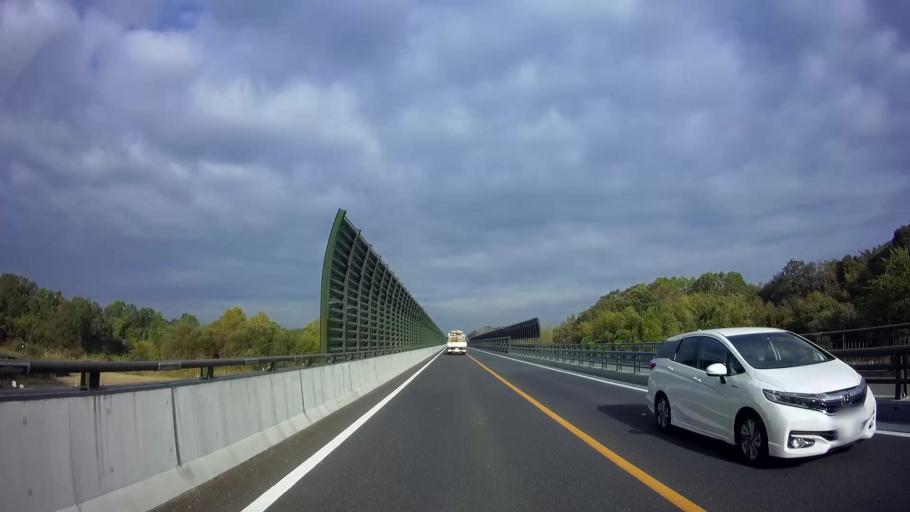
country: JP
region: Saitama
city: Okegawa
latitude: 35.9758
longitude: 139.5404
